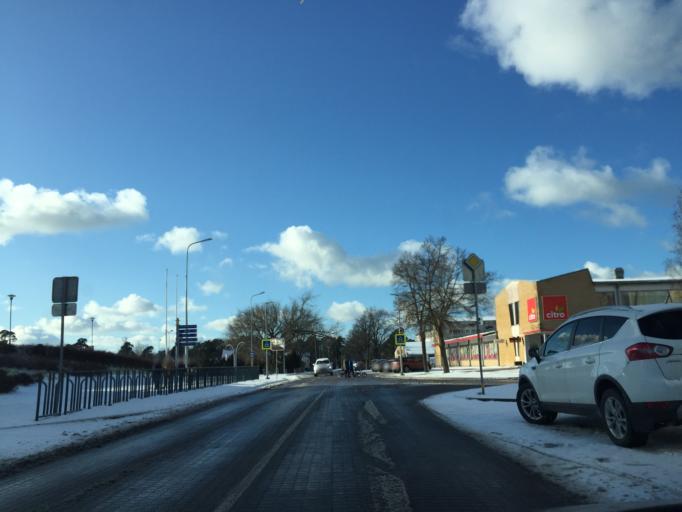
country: LV
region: Ventspils
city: Ventspils
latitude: 57.3853
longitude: 21.5471
